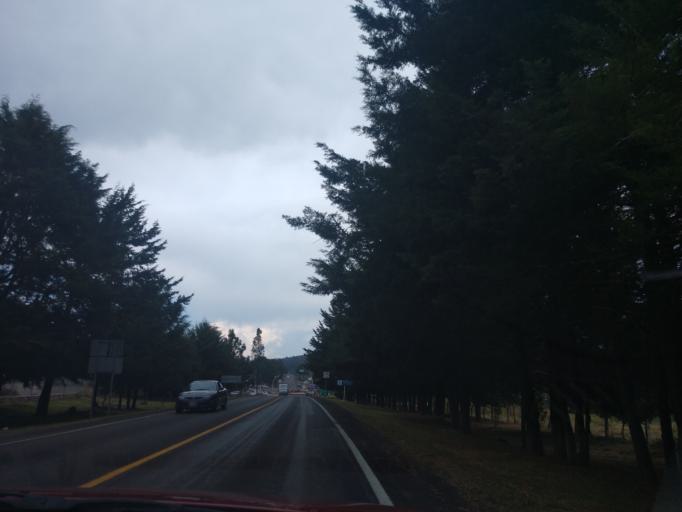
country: MX
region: Jalisco
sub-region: Mazamitla
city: Mazamitla
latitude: 19.9305
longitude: -103.0403
